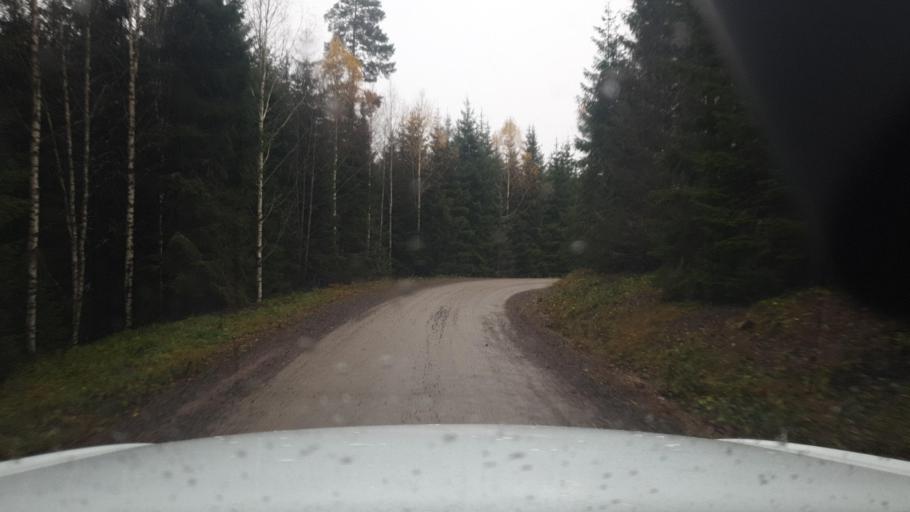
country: SE
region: Vaermland
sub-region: Arvika Kommun
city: Arvika
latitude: 59.9525
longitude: 12.6594
